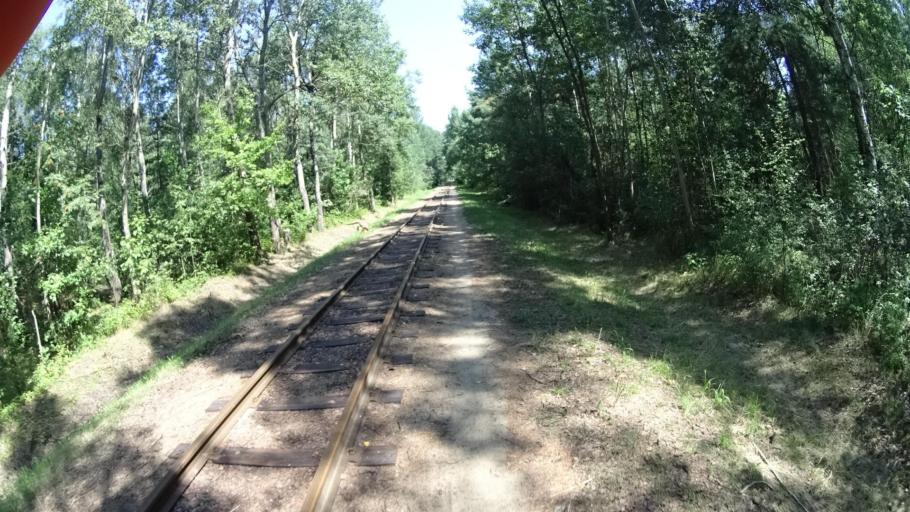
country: PL
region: Masovian Voivodeship
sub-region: Powiat piaseczynski
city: Tarczyn
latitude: 51.9876
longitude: 20.8841
